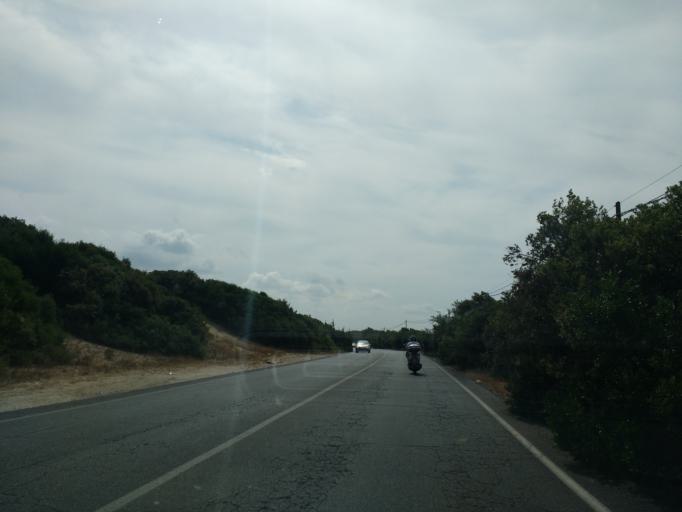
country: IT
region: Latium
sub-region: Citta metropolitana di Roma Capitale
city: Acilia-Castel Fusano-Ostia Antica
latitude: 41.6874
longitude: 12.3738
